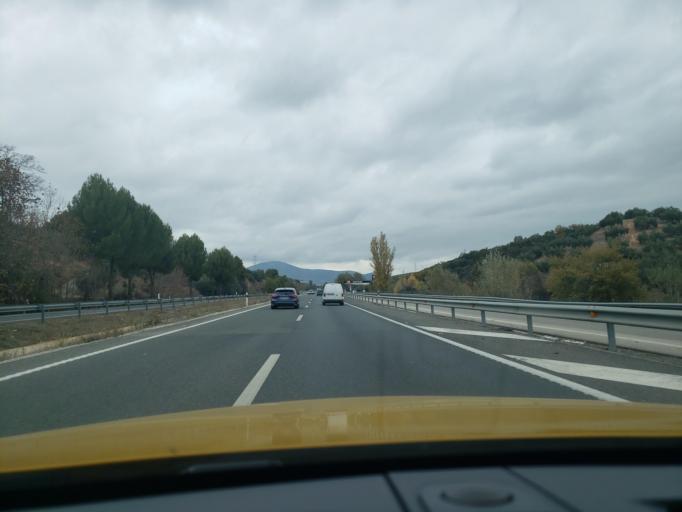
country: ES
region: Andalusia
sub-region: Provincia de Granada
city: Deifontes
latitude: 37.3419
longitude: -3.6207
